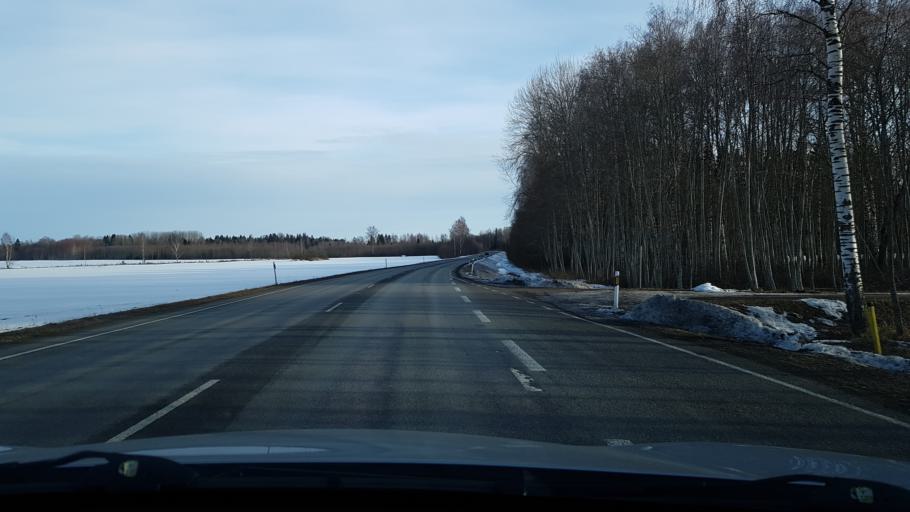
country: EE
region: Jogevamaa
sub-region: Poltsamaa linn
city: Poltsamaa
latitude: 58.3942
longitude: 25.9158
